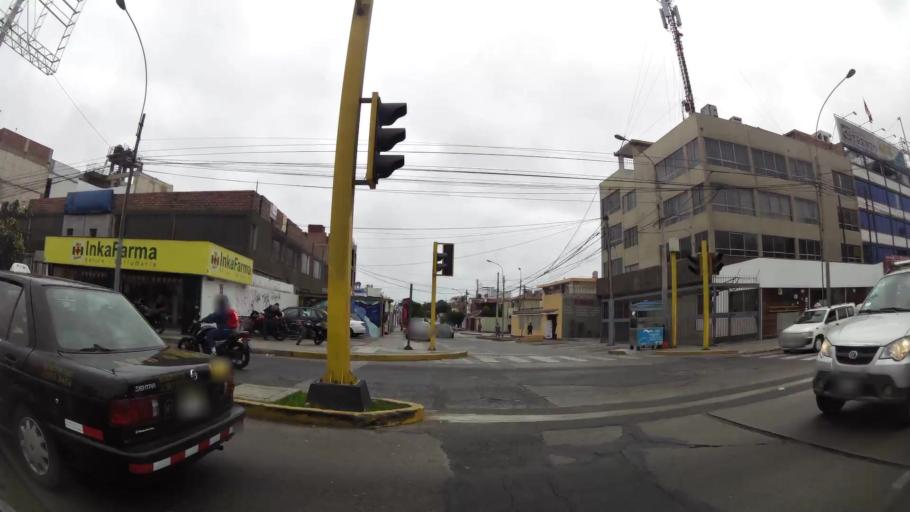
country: PE
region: Callao
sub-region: Callao
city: Callao
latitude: -12.0662
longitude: -77.0976
